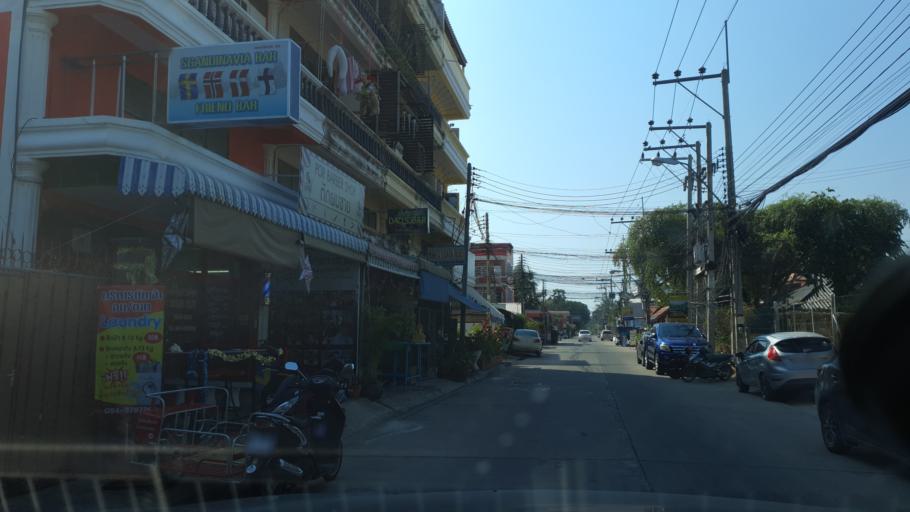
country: TH
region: Phetchaburi
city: Cha-am
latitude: 12.7927
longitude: 99.9812
